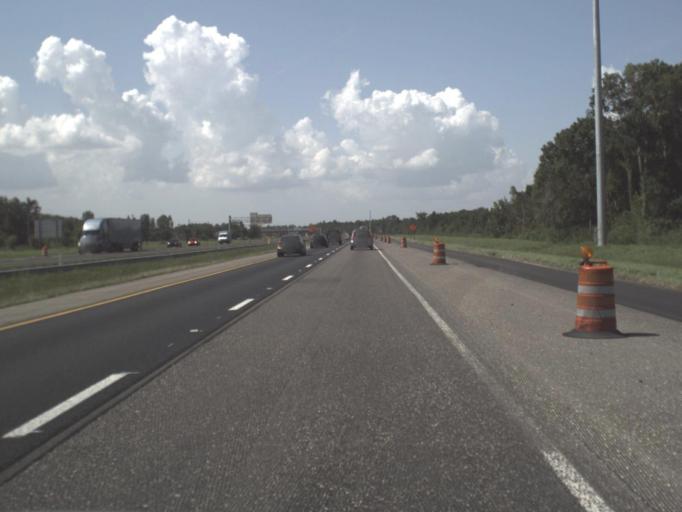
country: US
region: Florida
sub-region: Hillsborough County
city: Pebble Creek
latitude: 28.1319
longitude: -82.3775
